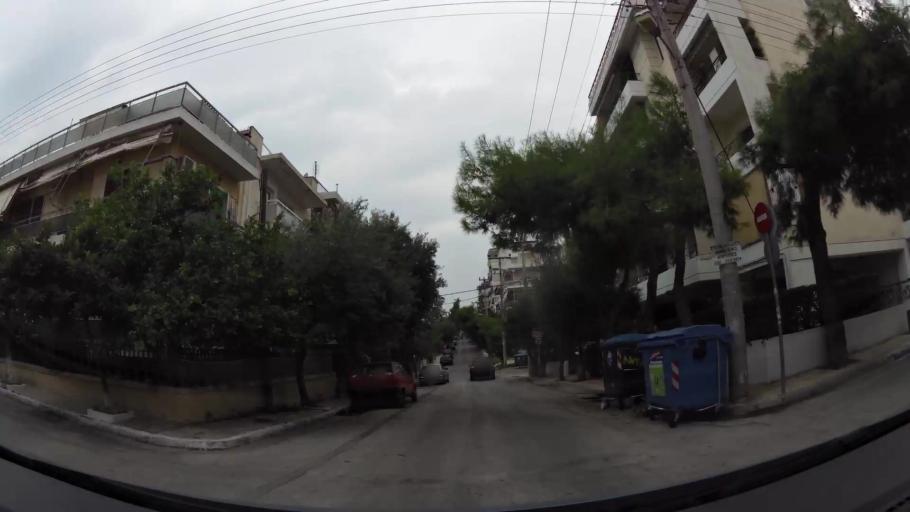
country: GR
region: Attica
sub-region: Nomarchia Athinas
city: Palaio Faliro
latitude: 37.9274
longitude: 23.7146
